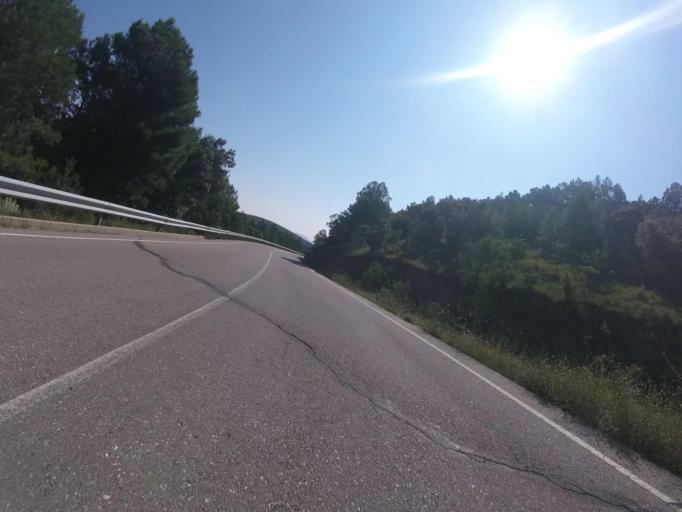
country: ES
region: Valencia
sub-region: Provincia de Castello
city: Benafigos
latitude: 40.2673
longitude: -0.2435
